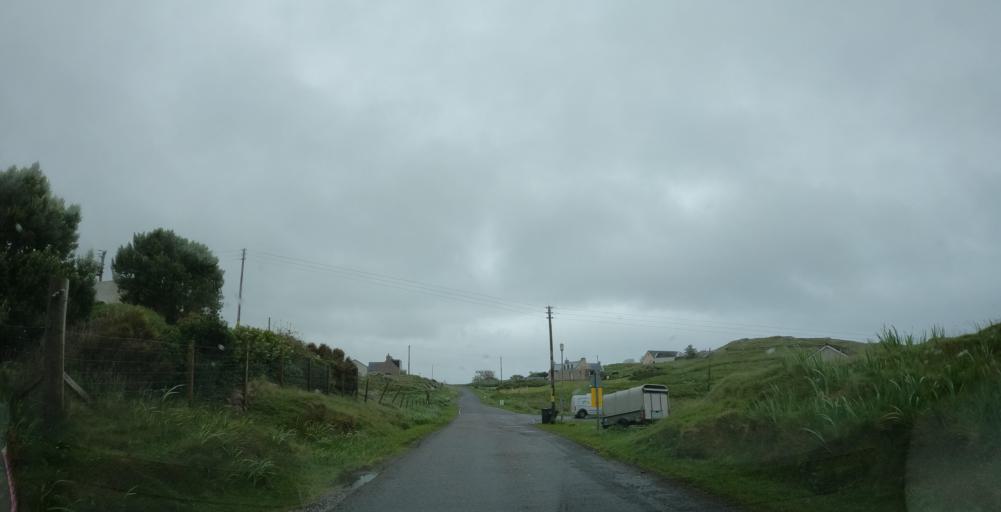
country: GB
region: Scotland
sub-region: Eilean Siar
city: Barra
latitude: 56.9645
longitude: -7.4373
